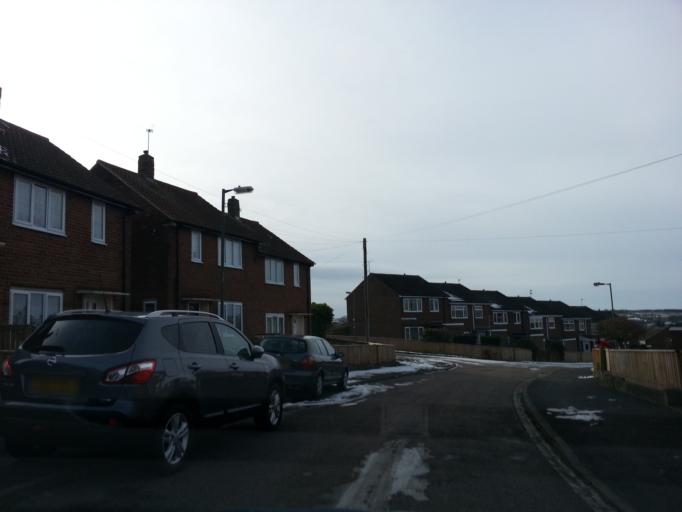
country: GB
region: England
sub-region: County Durham
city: Crook
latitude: 54.7079
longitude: -1.7394
